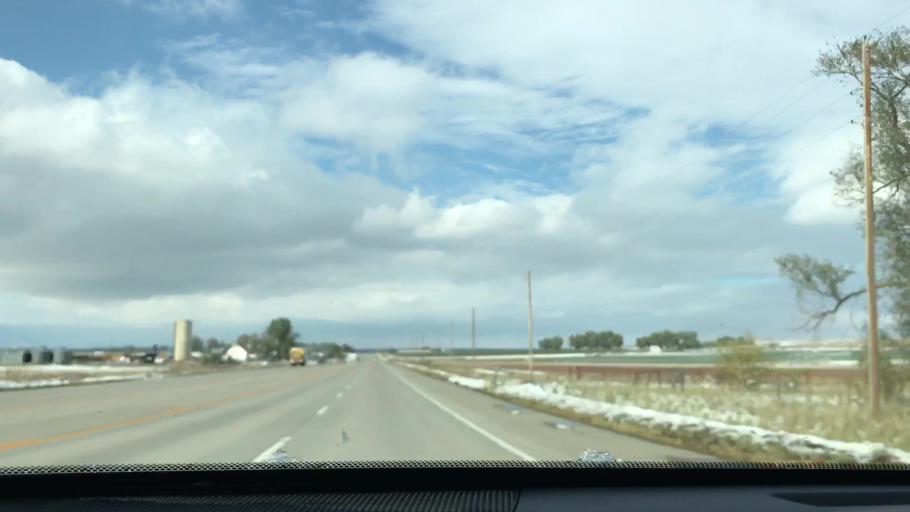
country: US
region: Colorado
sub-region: Boulder County
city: Longmont
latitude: 40.1077
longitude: -105.1015
